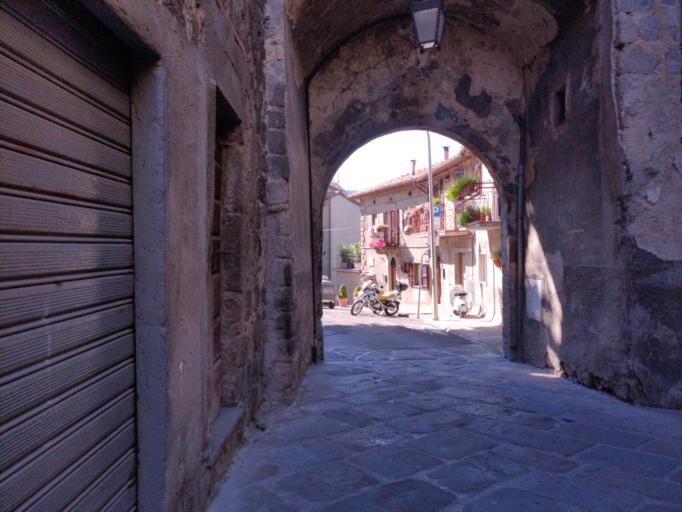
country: IT
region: Tuscany
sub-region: Provincia di Siena
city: Abbadia San Salvatore
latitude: 42.8816
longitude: 11.6780
